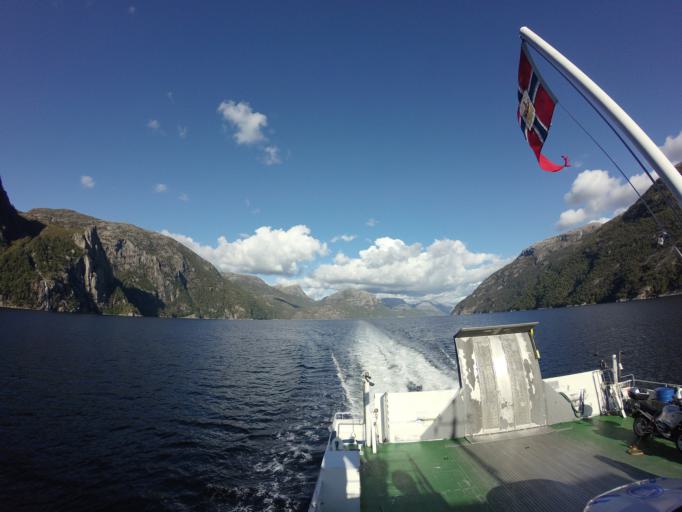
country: NO
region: Rogaland
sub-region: Forsand
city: Forsand
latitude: 58.9905
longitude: 6.2313
